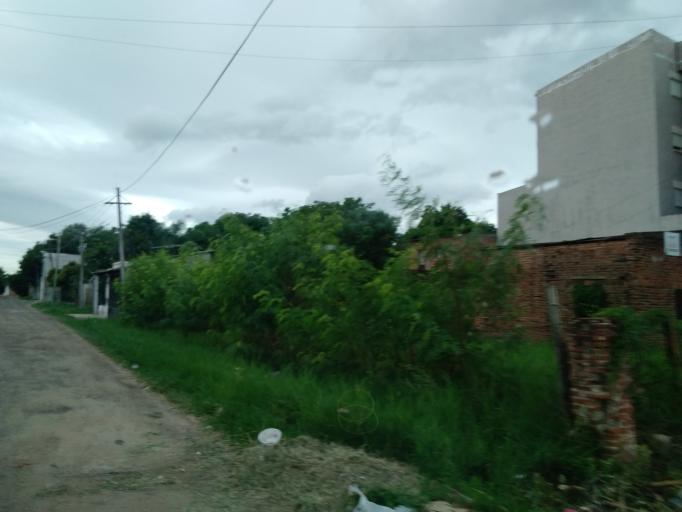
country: AR
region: Corrientes
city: Corrientes
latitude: -27.4804
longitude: -58.8255
